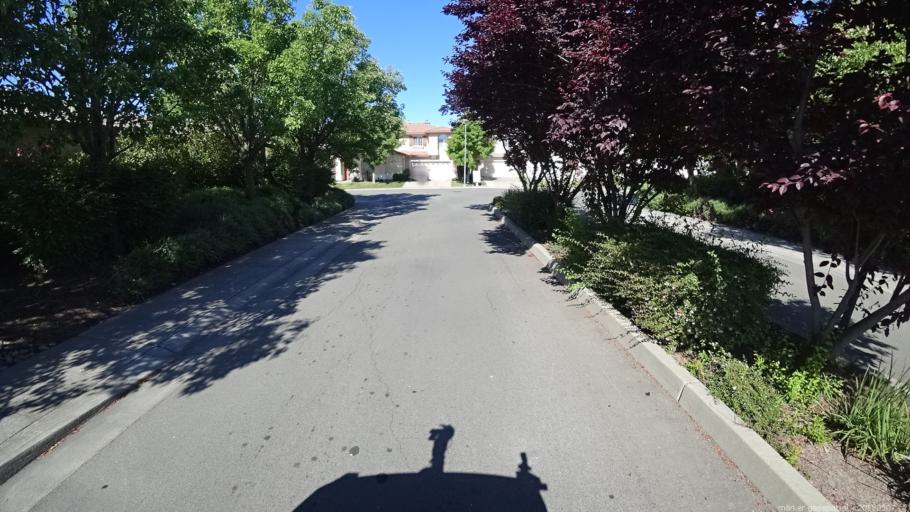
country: US
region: California
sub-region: Sacramento County
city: Rio Linda
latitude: 38.6577
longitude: -121.5031
